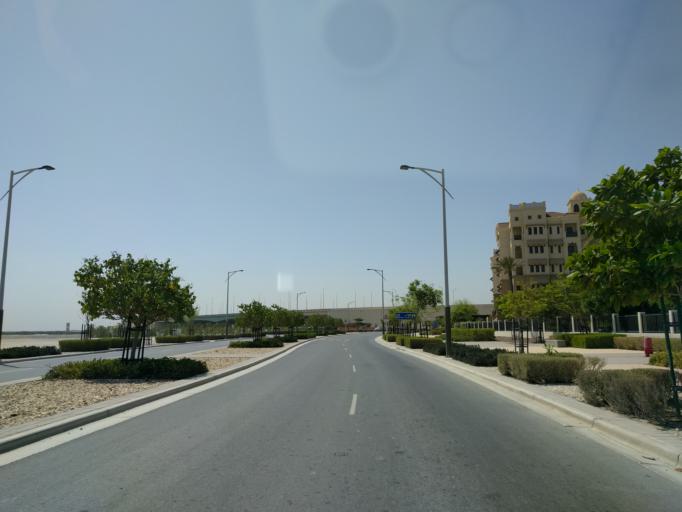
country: AE
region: Abu Dhabi
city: Abu Dhabi
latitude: 24.5513
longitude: 54.4534
